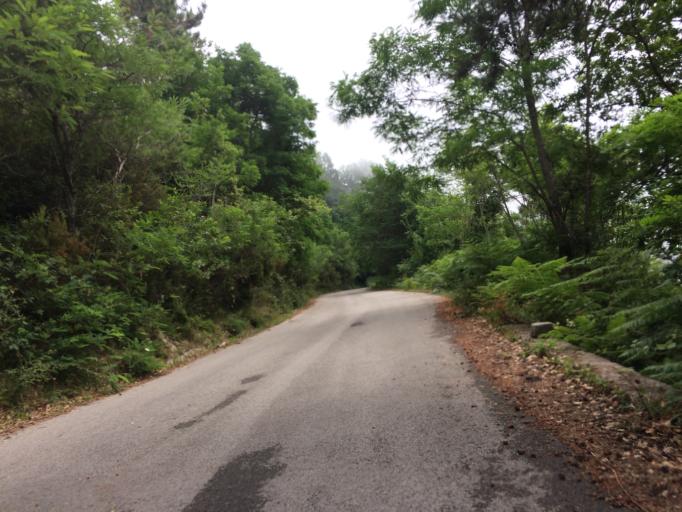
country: IT
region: Liguria
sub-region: Provincia di Imperia
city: Ceriana
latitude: 43.8608
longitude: 7.7414
